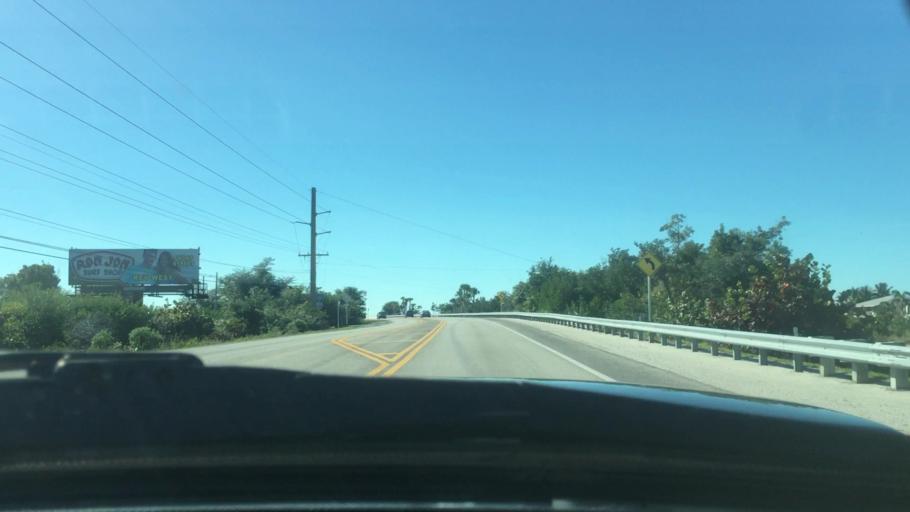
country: US
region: Florida
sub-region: Monroe County
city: Big Pine Key
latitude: 24.6699
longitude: -81.3690
